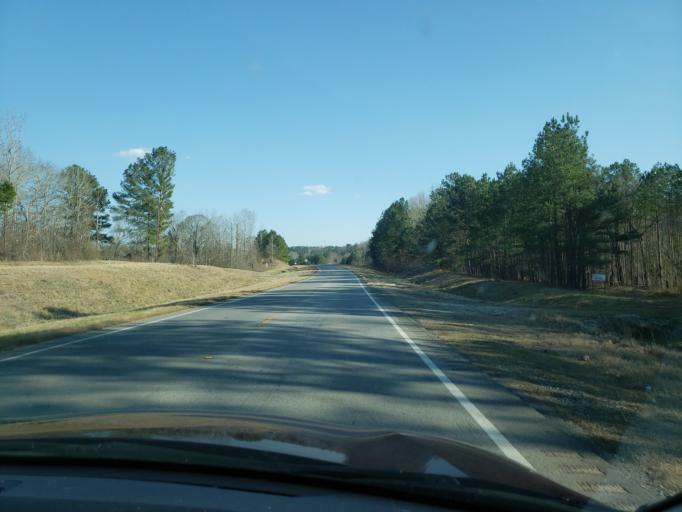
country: US
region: Alabama
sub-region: Cleburne County
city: Heflin
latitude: 33.5082
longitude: -85.6231
